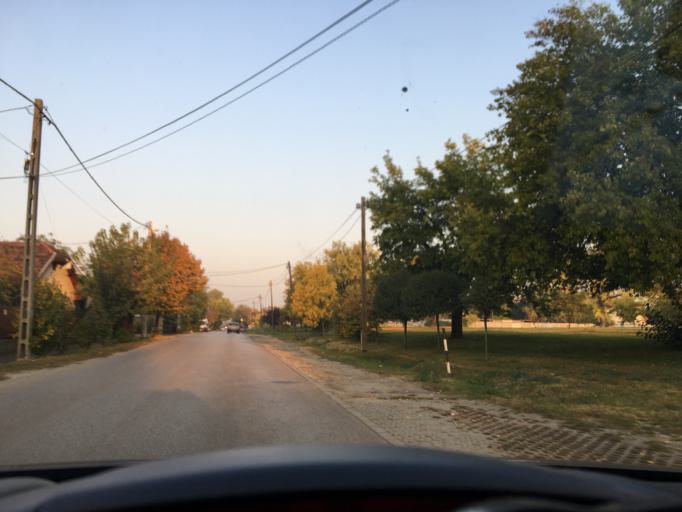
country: HU
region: Budapest
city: Budapest XVII. keruelet
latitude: 47.4759
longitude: 19.2491
